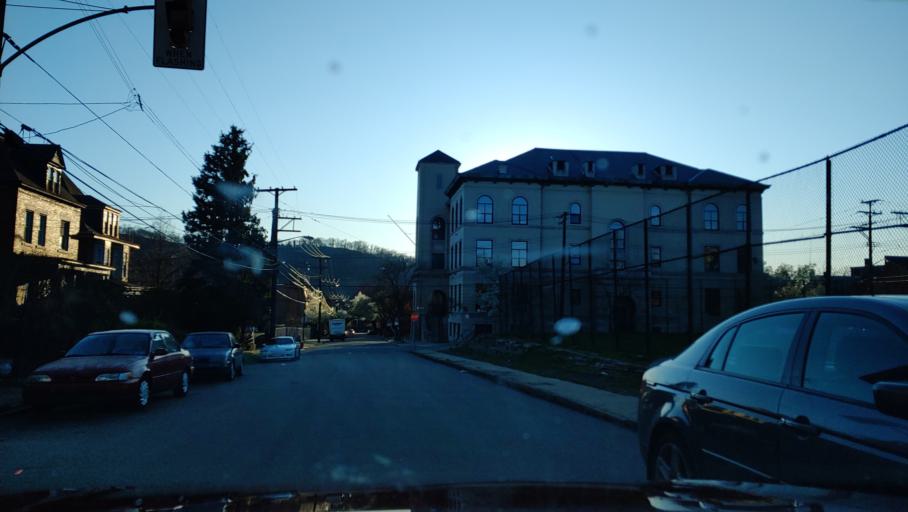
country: US
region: Pennsylvania
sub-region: Allegheny County
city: Pittsburgh
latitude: 40.4517
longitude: -80.0229
